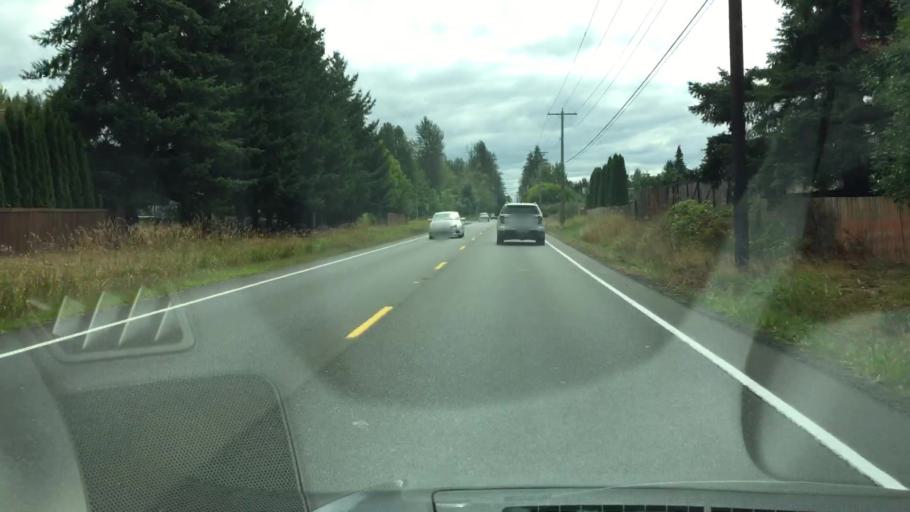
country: US
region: Washington
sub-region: Pierce County
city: South Hill
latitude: 47.1158
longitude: -122.2668
